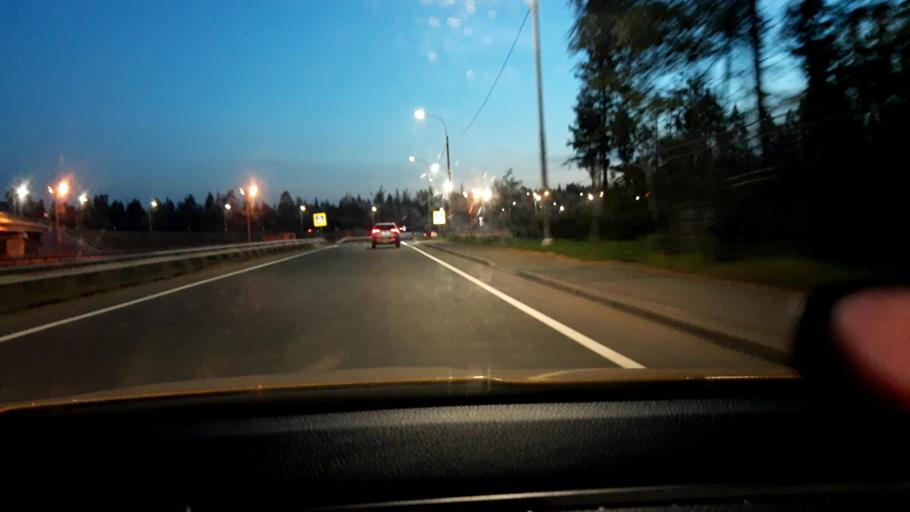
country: RU
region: Moskovskaya
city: Krasnoznamensk
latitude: 55.6078
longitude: 37.0536
